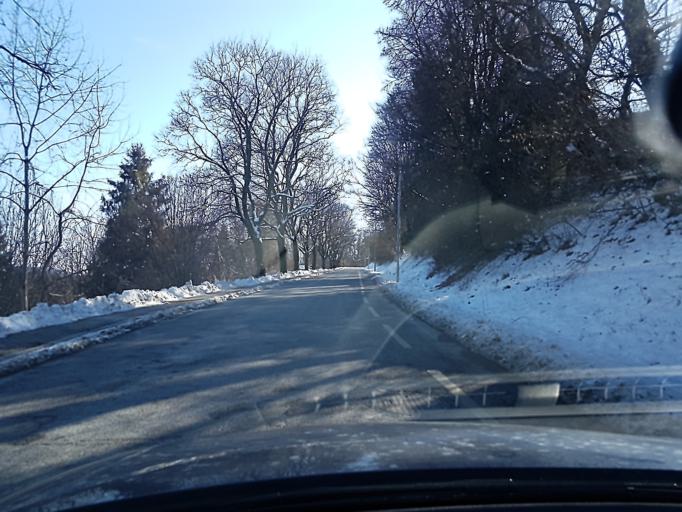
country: DE
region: Baden-Wuerttemberg
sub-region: Freiburg Region
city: Rottweil
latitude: 48.1748
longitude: 8.6264
